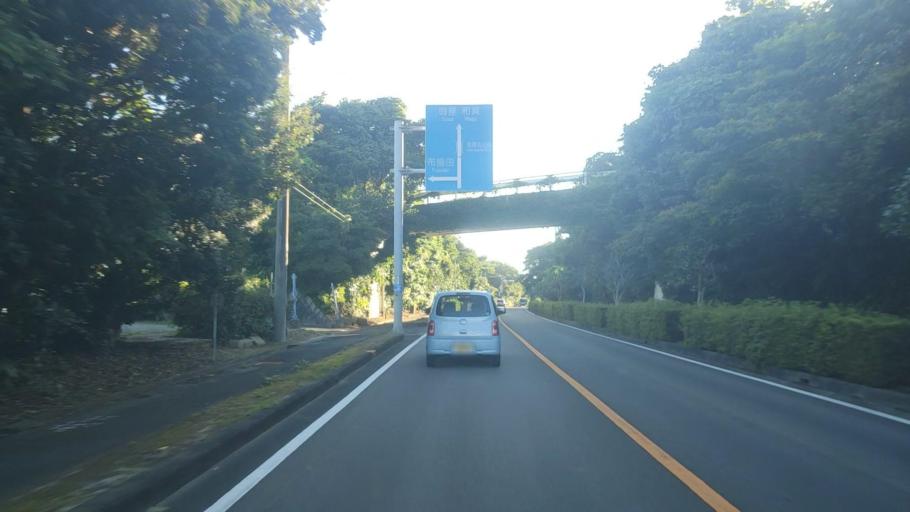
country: JP
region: Mie
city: Toba
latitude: 34.2604
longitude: 136.8402
